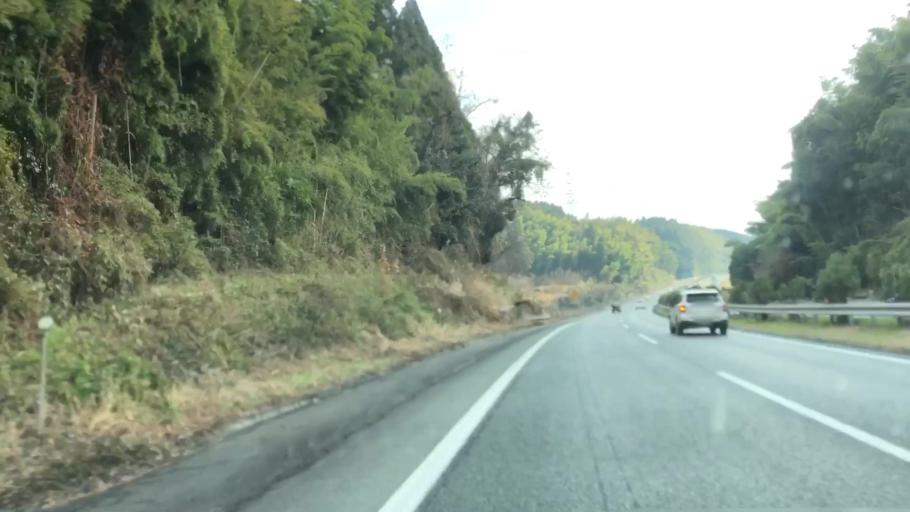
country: JP
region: Kumamoto
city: Yamaga
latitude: 33.0414
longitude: 130.5686
